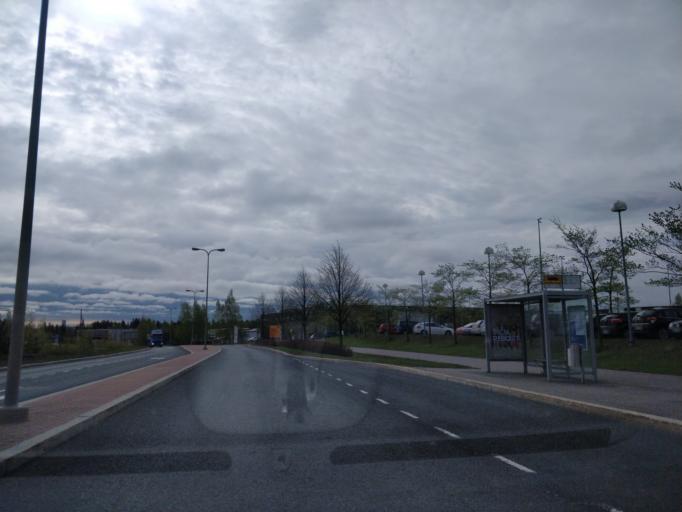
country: FI
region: Uusimaa
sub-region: Helsinki
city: Vantaa
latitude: 60.3018
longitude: 24.9253
